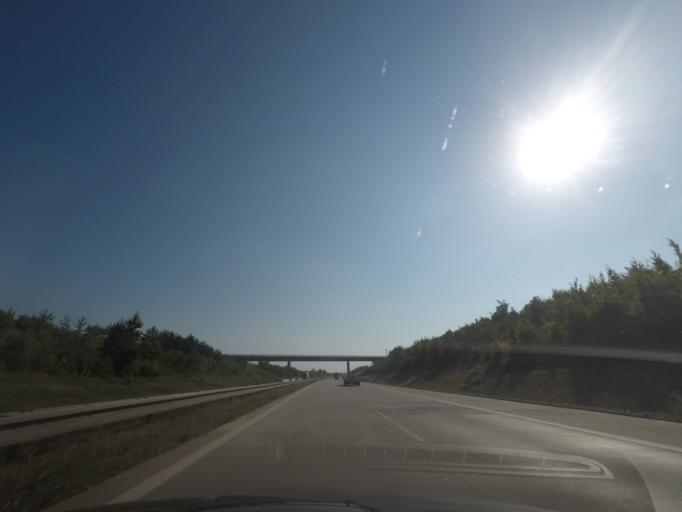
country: CZ
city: Bilovec
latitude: 49.7061
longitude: 17.9913
